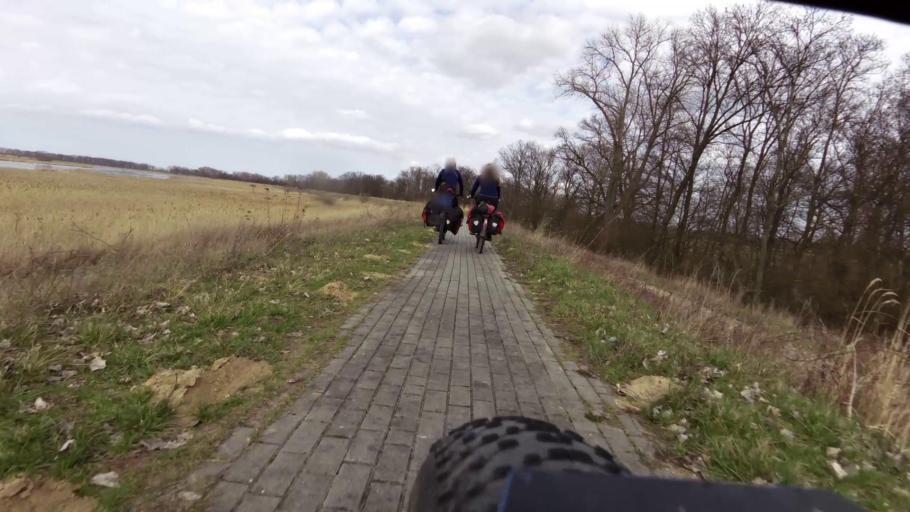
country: PL
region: Lubusz
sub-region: Powiat slubicki
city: Gorzyca
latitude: 52.4878
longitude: 14.6348
